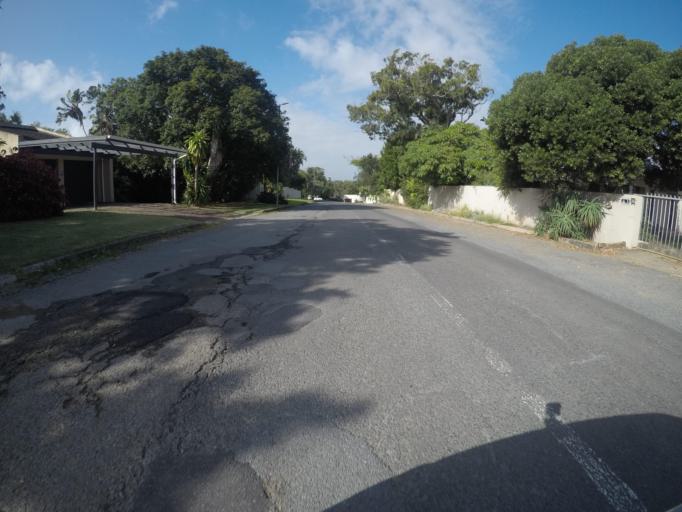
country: ZA
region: Eastern Cape
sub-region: Buffalo City Metropolitan Municipality
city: East London
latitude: -32.9724
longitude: 27.9584
